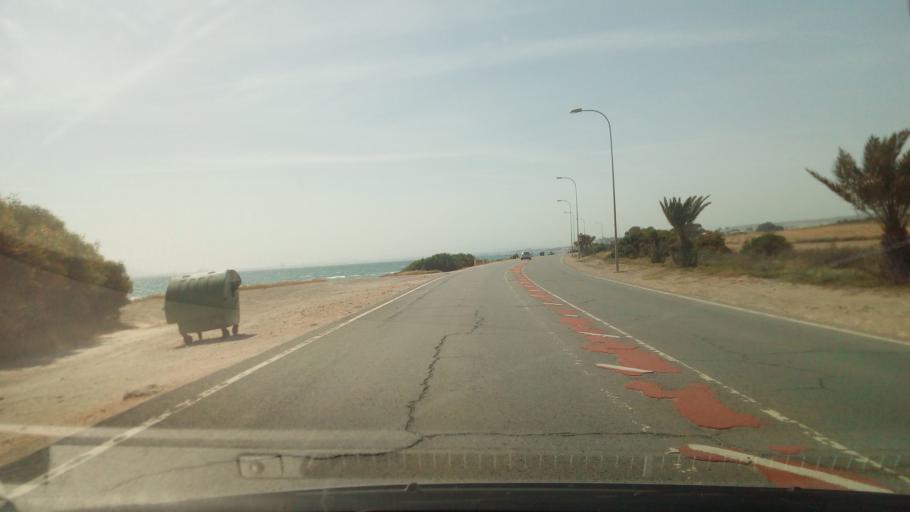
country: CY
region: Larnaka
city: Pyla
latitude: 34.9807
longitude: 33.7129
